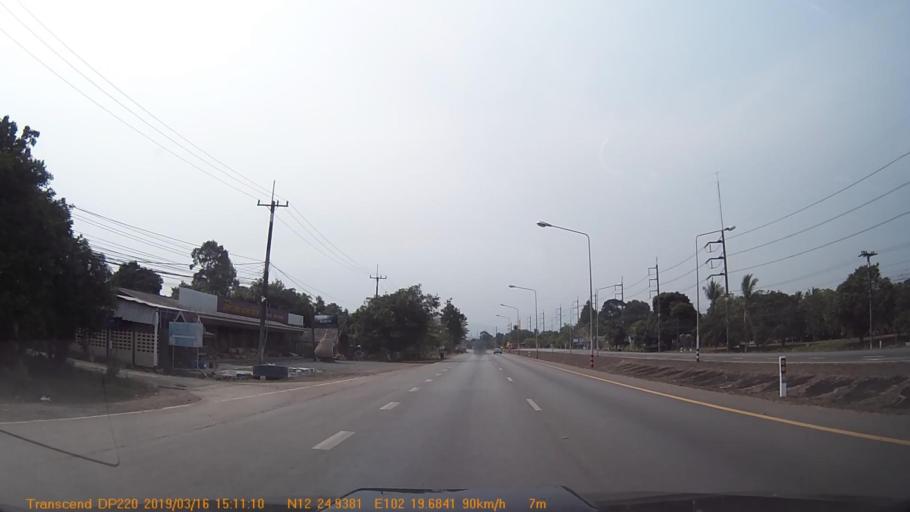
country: TH
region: Chanthaburi
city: Khlung
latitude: 12.4160
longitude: 102.3278
